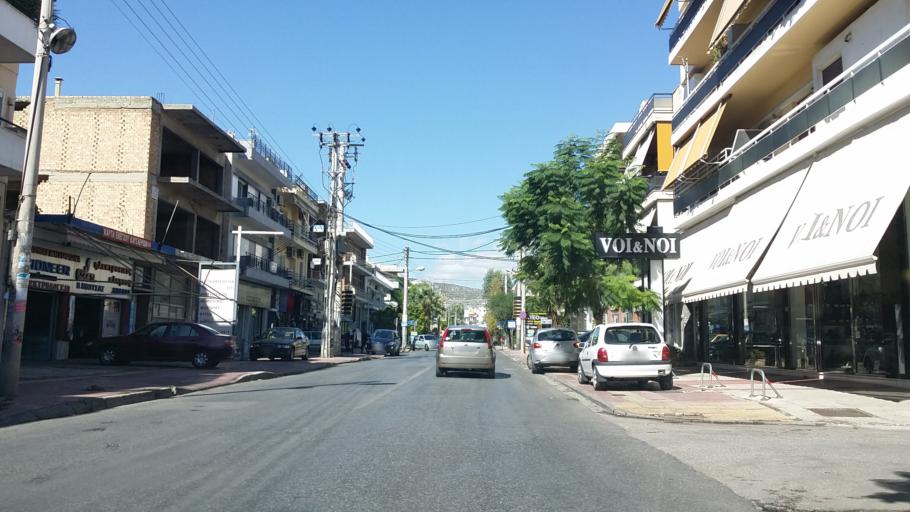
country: GR
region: Attica
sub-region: Nomarchia Athinas
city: Agioi Anargyroi
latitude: 38.0288
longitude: 23.7157
